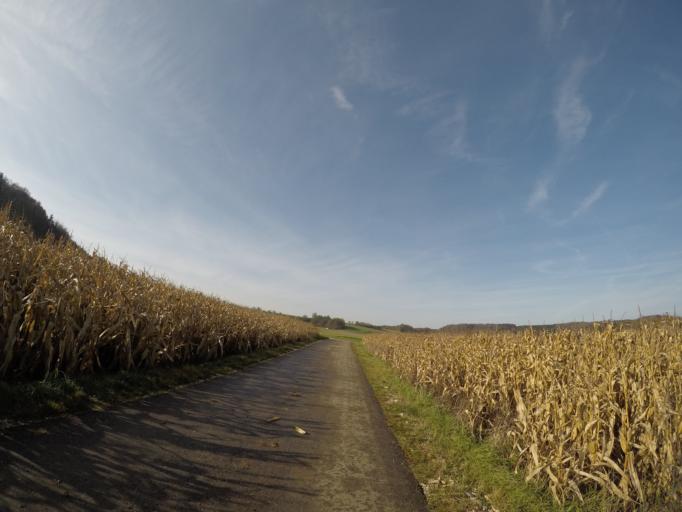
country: DE
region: Baden-Wuerttemberg
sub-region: Tuebingen Region
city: Bernstadt
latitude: 48.4872
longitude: 10.0074
